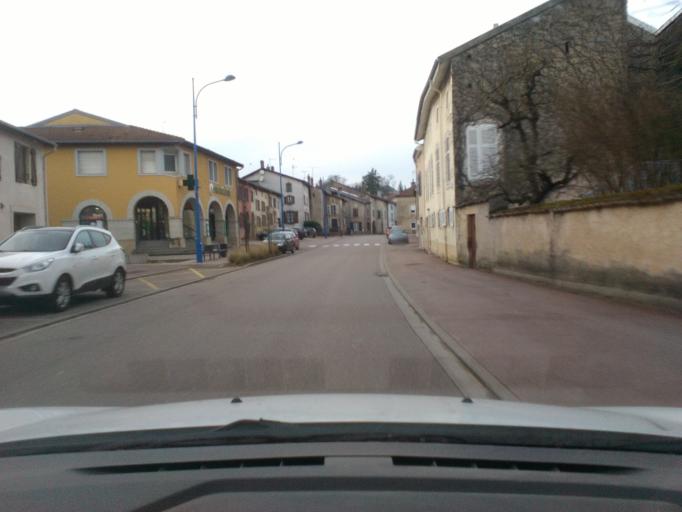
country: FR
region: Lorraine
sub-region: Departement des Vosges
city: Mirecourt
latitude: 48.2774
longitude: 6.1342
